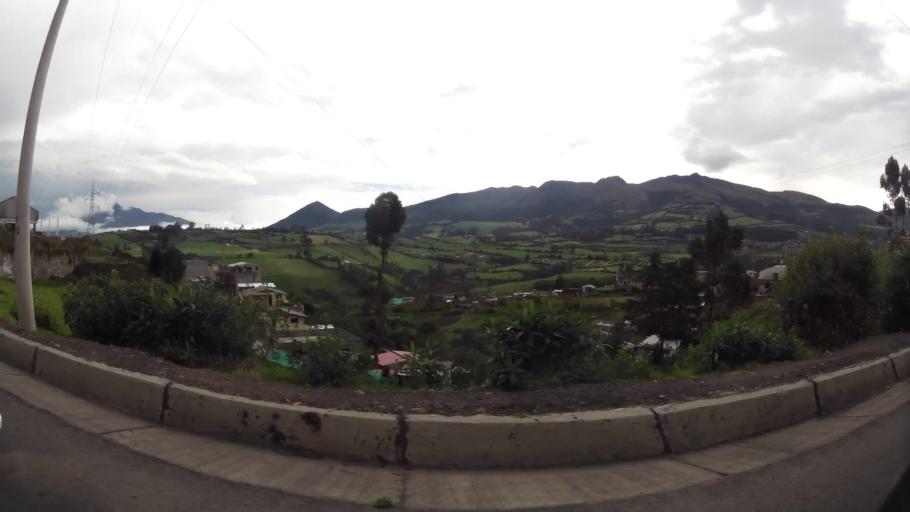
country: EC
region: Pichincha
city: Sangolqui
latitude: -0.3858
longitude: -78.5497
